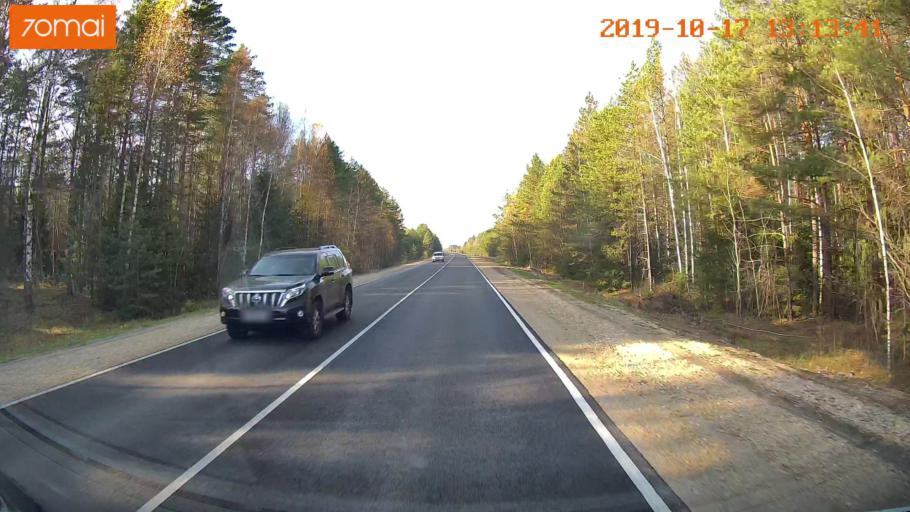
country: RU
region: Rjazan
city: Gus'-Zheleznyy
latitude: 55.0469
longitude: 41.1862
